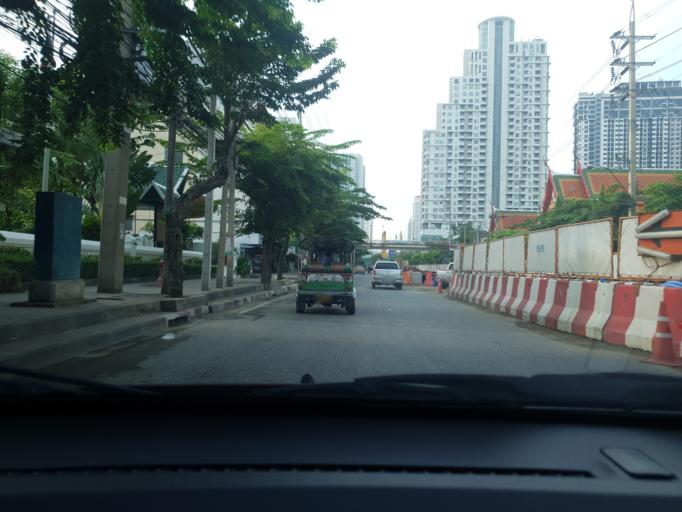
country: TH
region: Bangkok
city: Khlong San
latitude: 13.7248
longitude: 100.5092
